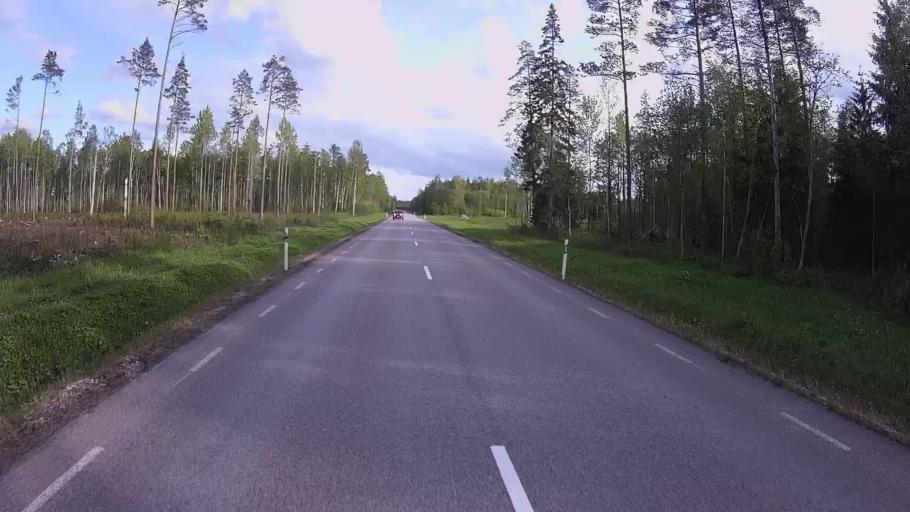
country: EE
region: Jogevamaa
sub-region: Mustvee linn
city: Mustvee
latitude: 59.0714
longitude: 26.9981
